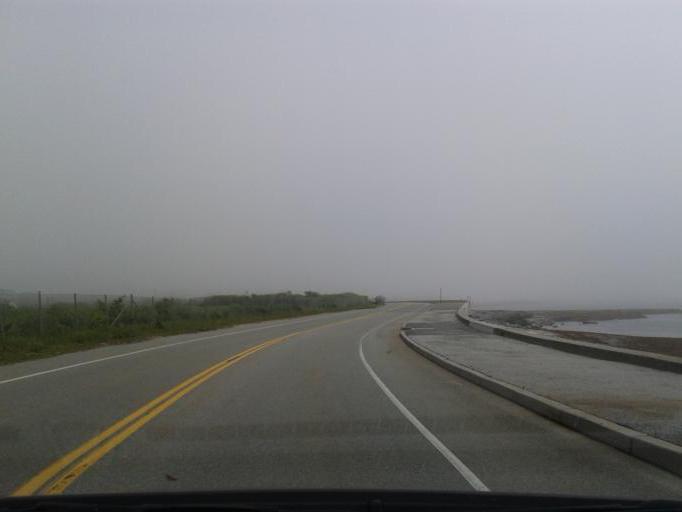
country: US
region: Rhode Island
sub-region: Newport County
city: Jamestown
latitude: 41.4515
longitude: -71.3512
